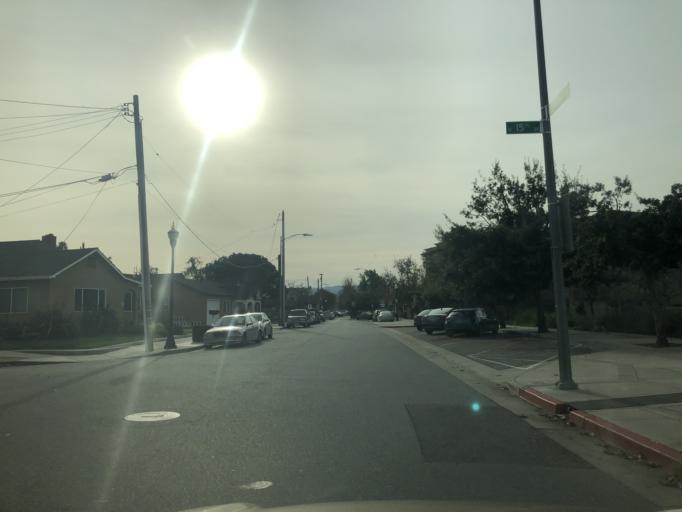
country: US
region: California
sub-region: Santa Clara County
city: San Jose
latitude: 37.3609
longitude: -121.8896
